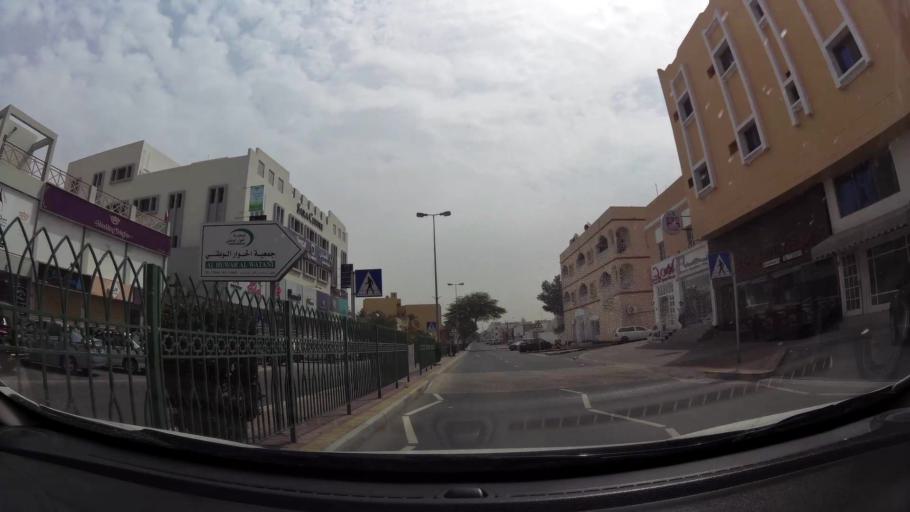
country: BH
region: Northern
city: Ar Rifa'
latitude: 26.1298
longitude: 50.5410
